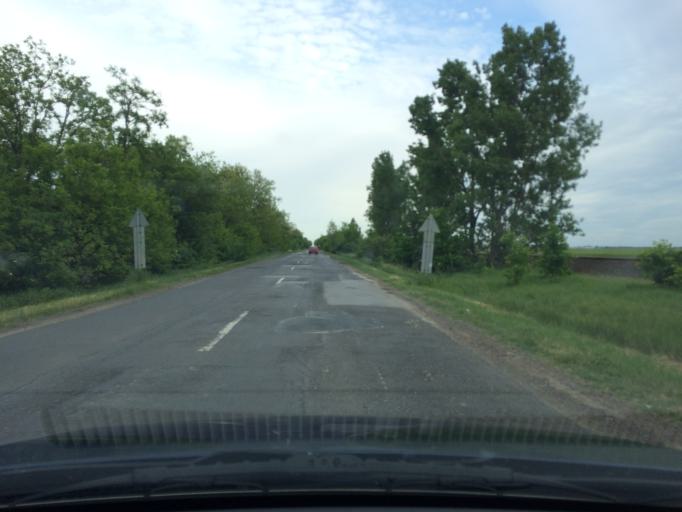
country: HU
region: Szabolcs-Szatmar-Bereg
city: Tiszavasvari
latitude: 47.9189
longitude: 21.3950
